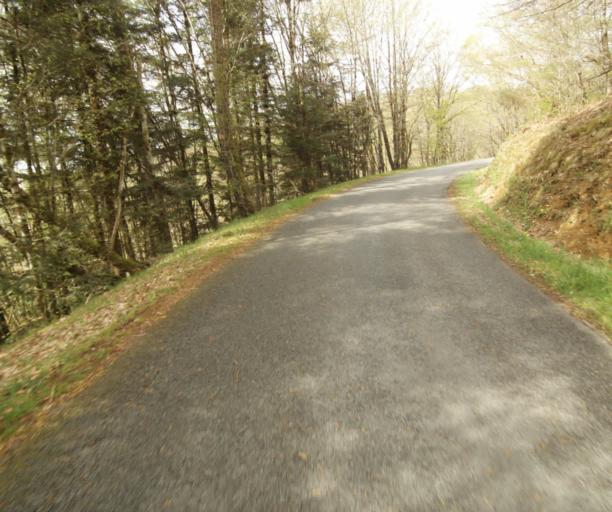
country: FR
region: Limousin
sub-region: Departement de la Correze
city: Laguenne
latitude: 45.2590
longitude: 1.8268
